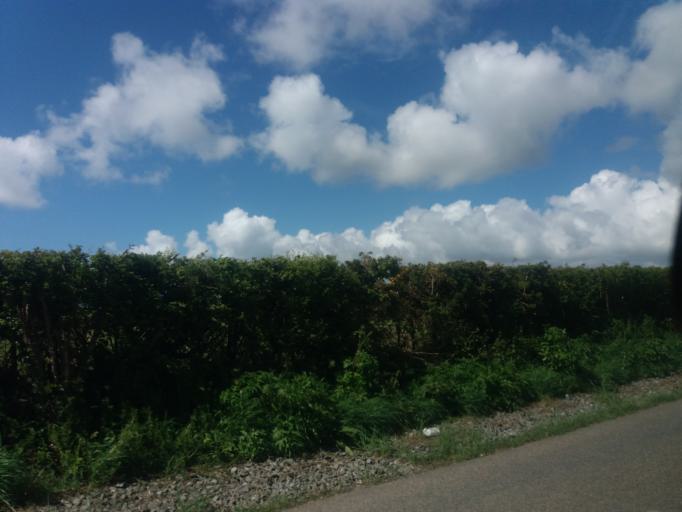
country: IE
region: Munster
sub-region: Waterford
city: Dunmore East
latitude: 52.2399
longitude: -6.8559
